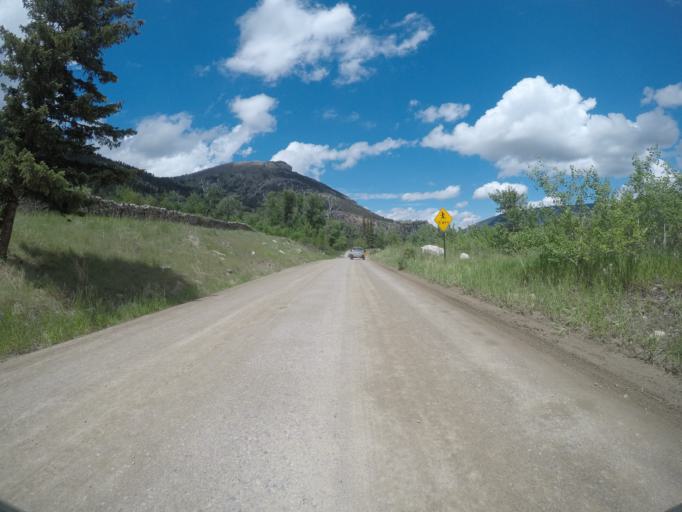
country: US
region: Montana
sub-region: Park County
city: Livingston
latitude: 45.5207
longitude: -110.2250
